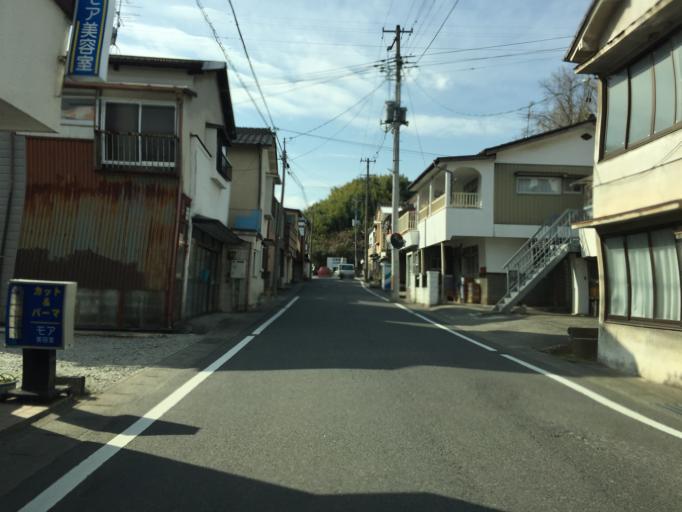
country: JP
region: Fukushima
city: Iwaki
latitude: 37.0063
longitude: 140.8382
